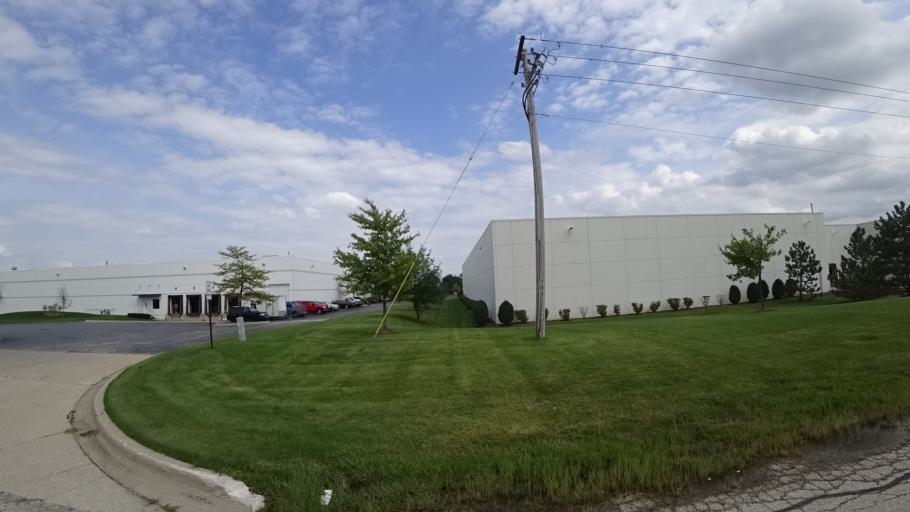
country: US
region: Illinois
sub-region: Cook County
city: Tinley Park
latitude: 41.5544
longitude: -87.8023
